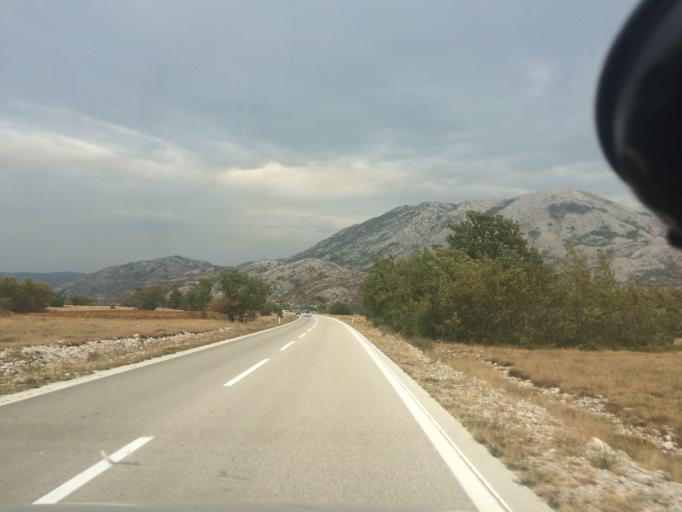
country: ME
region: Kotor
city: Risan
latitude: 42.5913
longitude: 18.6890
